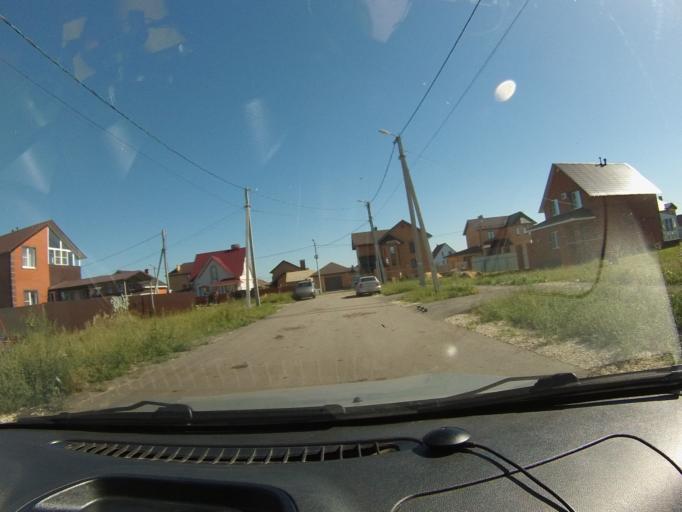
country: RU
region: Tambov
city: Tambov
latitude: 52.7701
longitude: 41.3745
